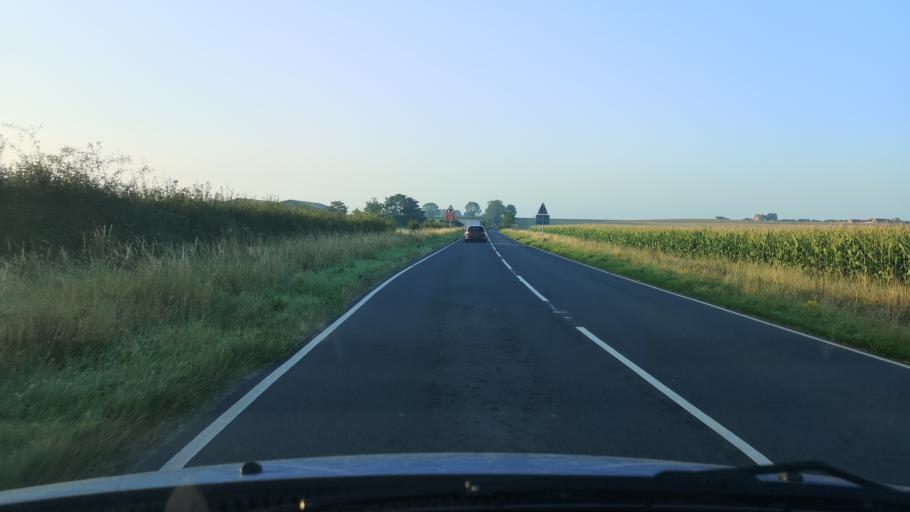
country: GB
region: England
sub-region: North Lincolnshire
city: Crowle
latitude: 53.6168
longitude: -0.8187
